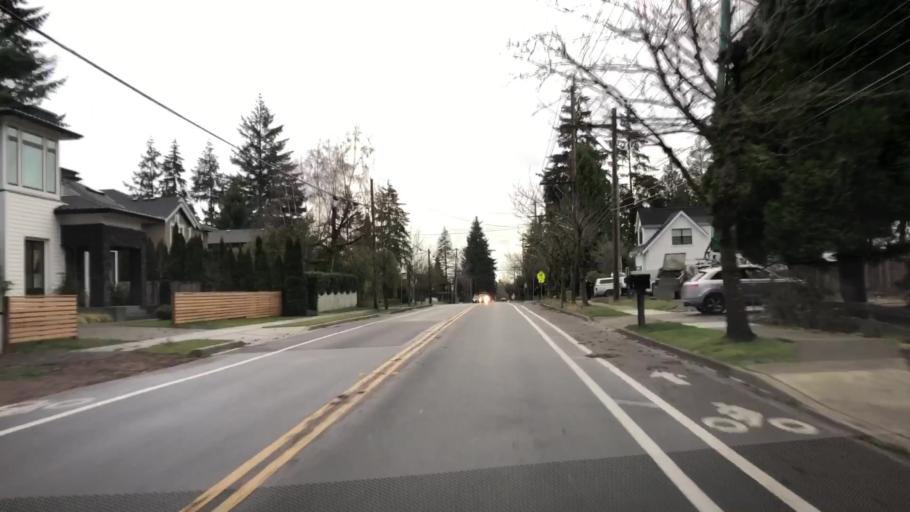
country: US
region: Washington
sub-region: King County
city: Kirkland
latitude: 47.6753
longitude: -122.1708
